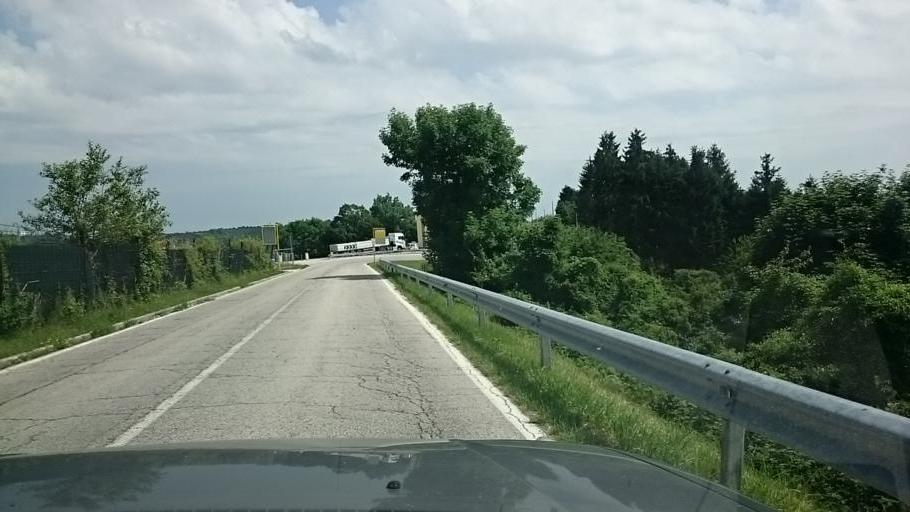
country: IT
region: Veneto
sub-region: Provincia di Vicenza
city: Conco
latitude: 45.8038
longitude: 11.6225
